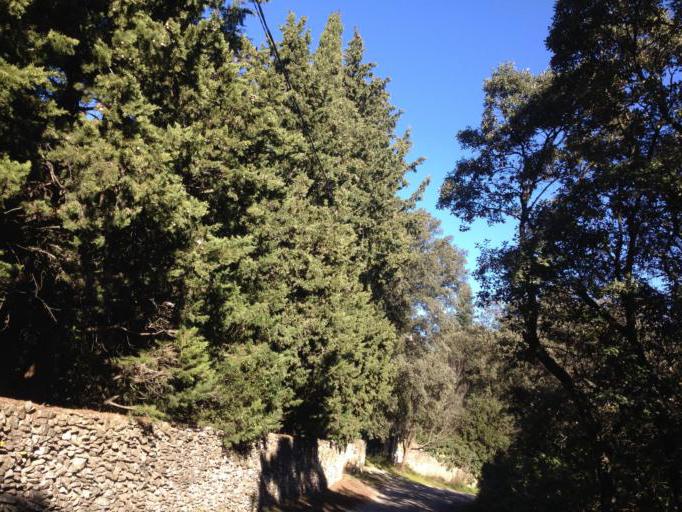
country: FR
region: Provence-Alpes-Cote d'Azur
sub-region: Departement du Vaucluse
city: Orange
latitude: 44.1279
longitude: 4.8077
